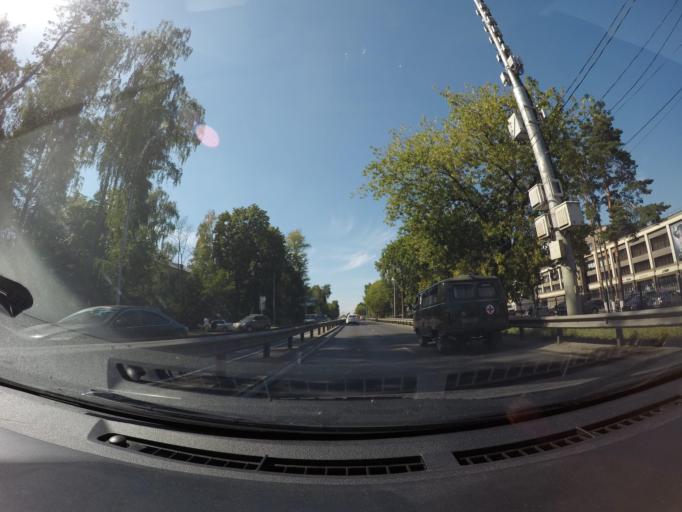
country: RU
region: Moskovskaya
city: Tomilino
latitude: 55.6624
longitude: 37.9553
